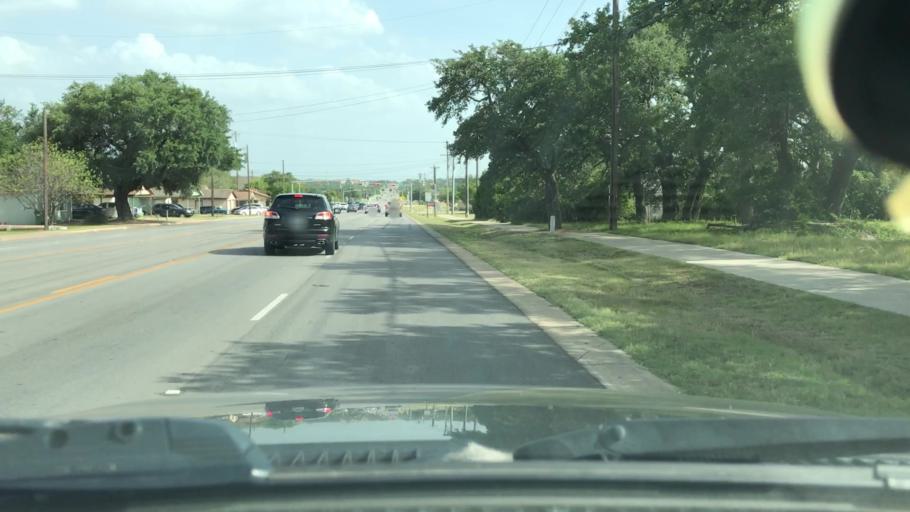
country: US
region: Texas
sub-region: Williamson County
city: Leander
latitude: 30.5431
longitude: -97.8506
